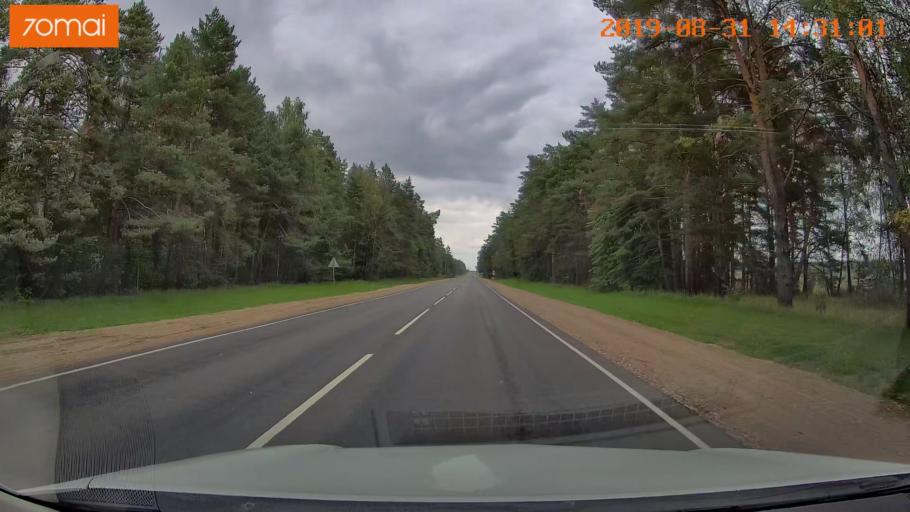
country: RU
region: Smolensk
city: Yekimovichi
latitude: 54.1355
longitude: 33.3641
